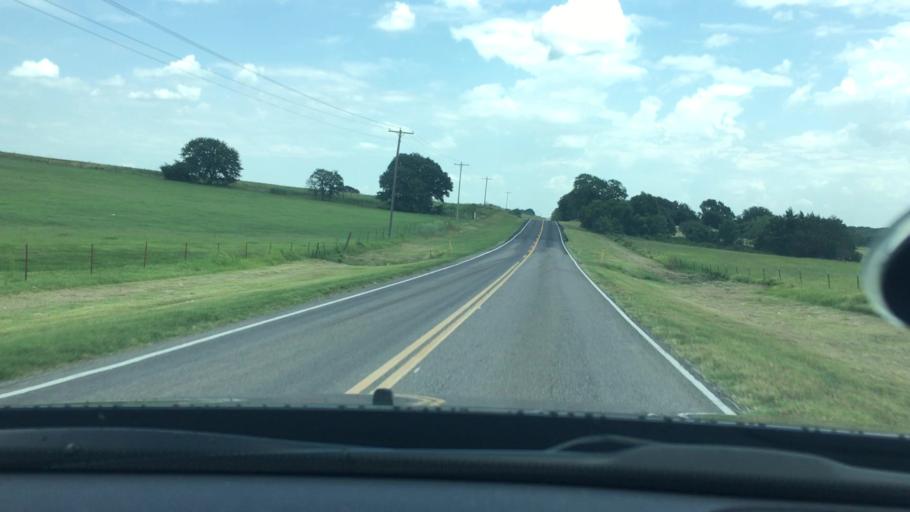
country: US
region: Oklahoma
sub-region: Carter County
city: Wilson
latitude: 33.9403
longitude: -97.3714
